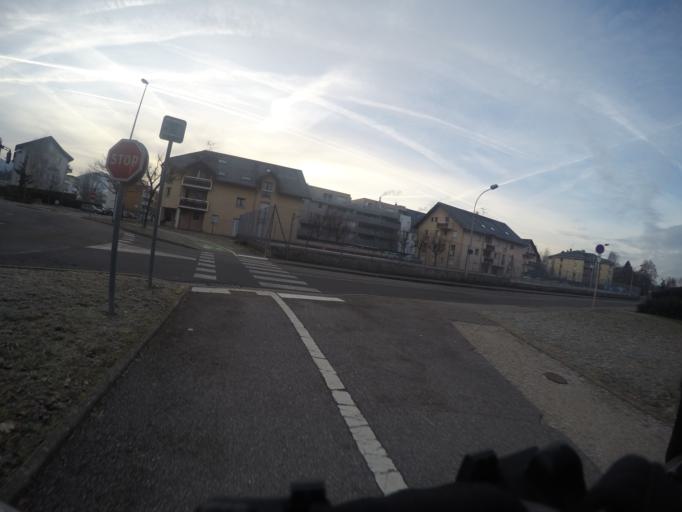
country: FR
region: Rhone-Alpes
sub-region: Departement de la Haute-Savoie
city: Meythet
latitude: 45.9170
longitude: 6.0880
